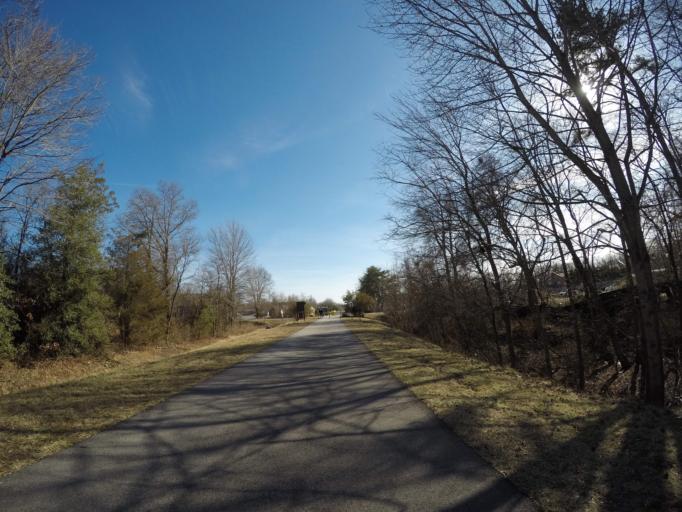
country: US
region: Maryland
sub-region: Charles County
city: Saint Charles
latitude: 38.5925
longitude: -76.9479
